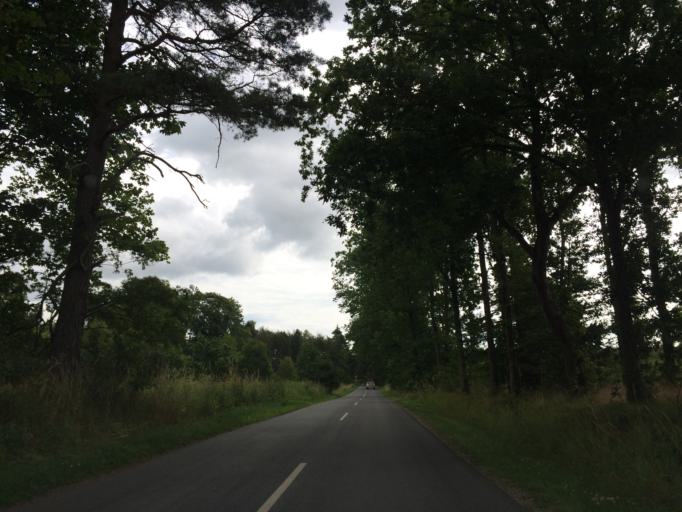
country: DK
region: Central Jutland
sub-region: Syddjurs Kommune
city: Ebeltoft
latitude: 56.2739
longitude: 10.7230
